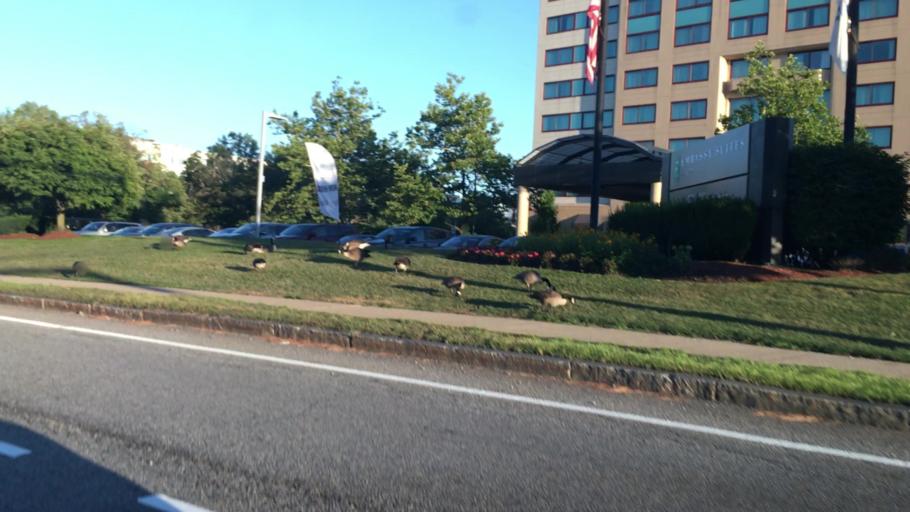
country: US
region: Massachusetts
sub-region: Middlesex County
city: Waltham
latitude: 42.3970
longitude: -71.2664
